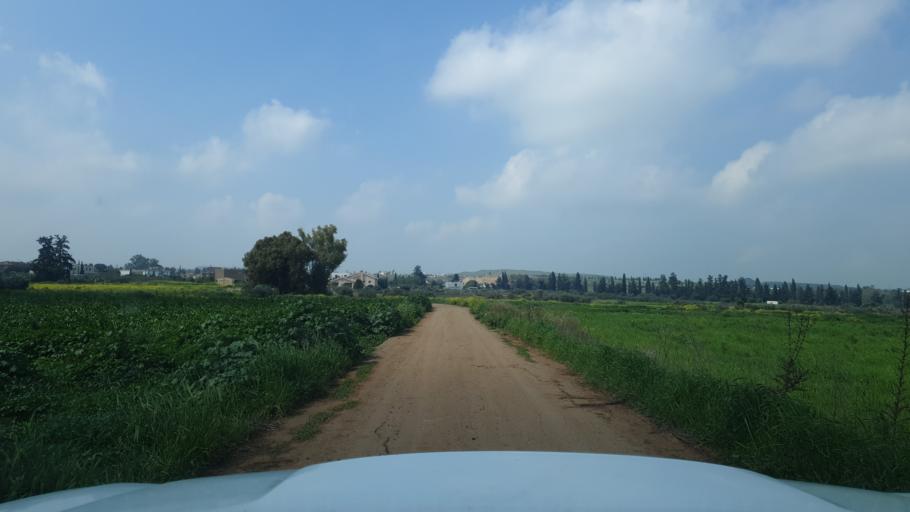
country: CY
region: Lefkosia
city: Kato Deftera
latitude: 35.0871
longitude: 33.2944
